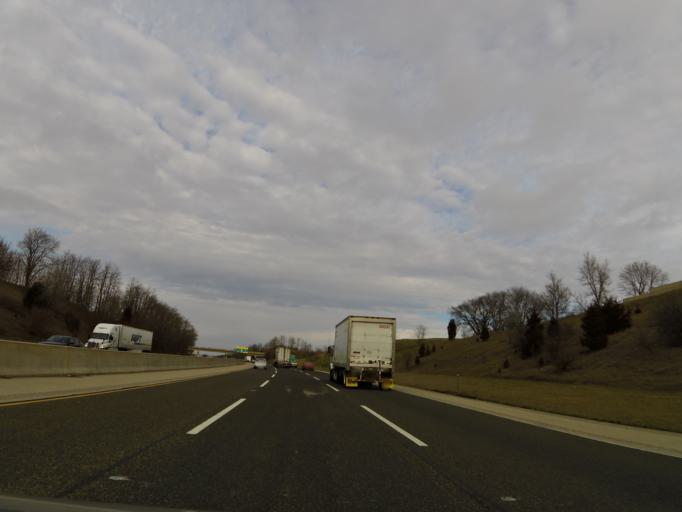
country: US
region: Illinois
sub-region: Winnebago County
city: Roscoe
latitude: 42.4247
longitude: -88.9856
